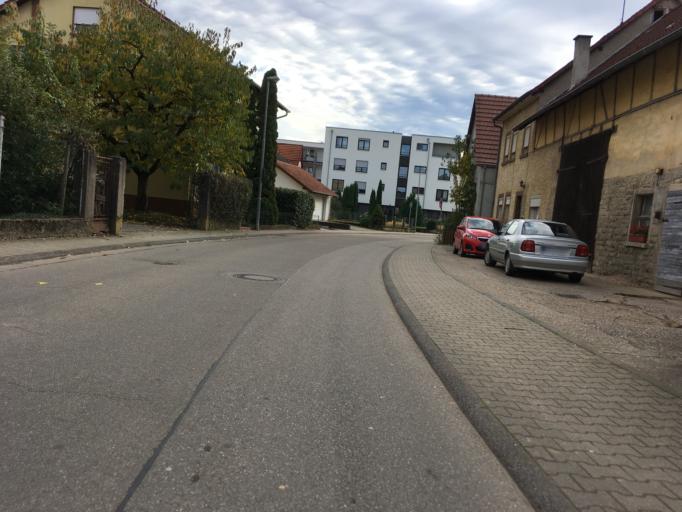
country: DE
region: Baden-Wuerttemberg
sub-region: Karlsruhe Region
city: Sinsheim
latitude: 49.2526
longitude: 8.9044
